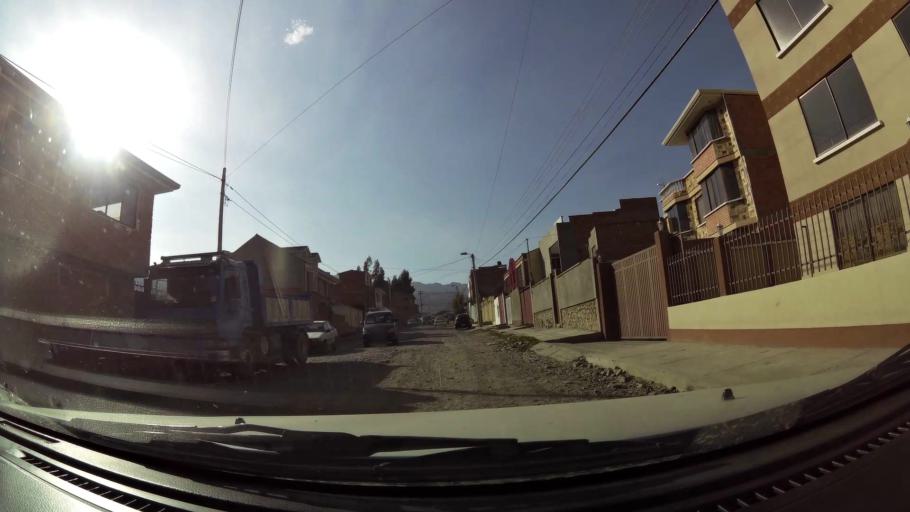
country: BO
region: La Paz
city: La Paz
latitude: -16.5180
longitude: -68.0843
